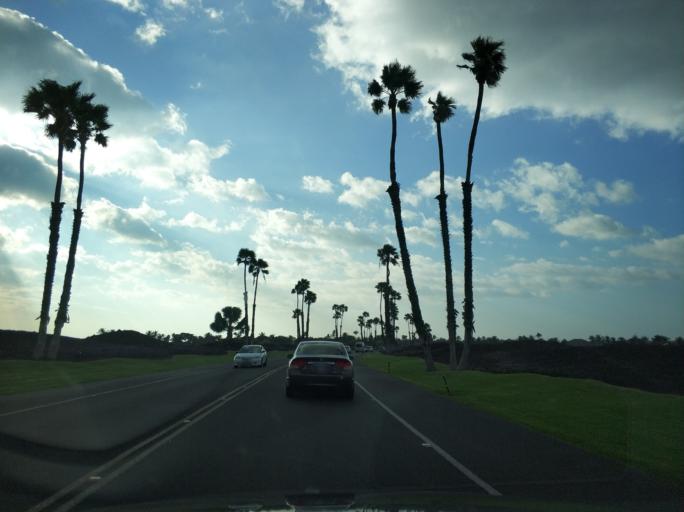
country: US
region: Hawaii
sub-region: Hawaii County
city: Waikoloa Village
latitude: 19.9130
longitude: -155.8744
